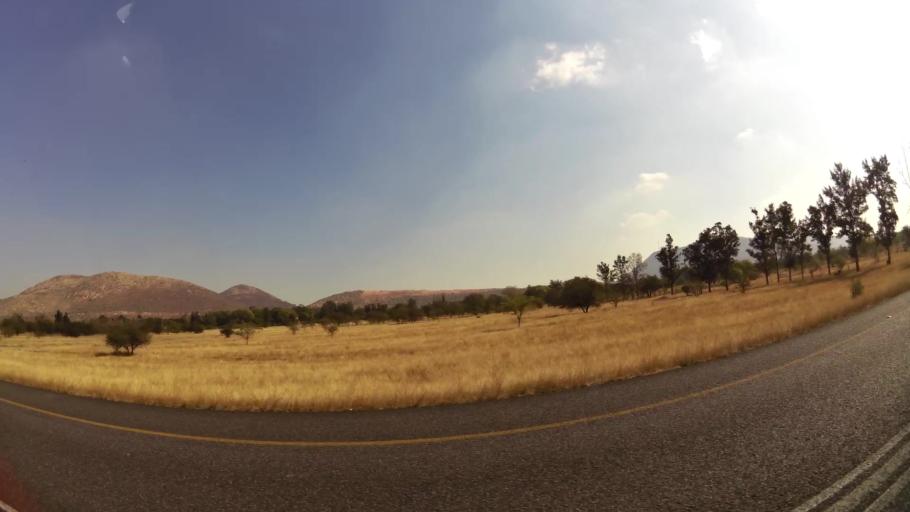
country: ZA
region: North-West
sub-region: Bojanala Platinum District Municipality
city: Rustenburg
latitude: -25.6248
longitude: 27.1574
